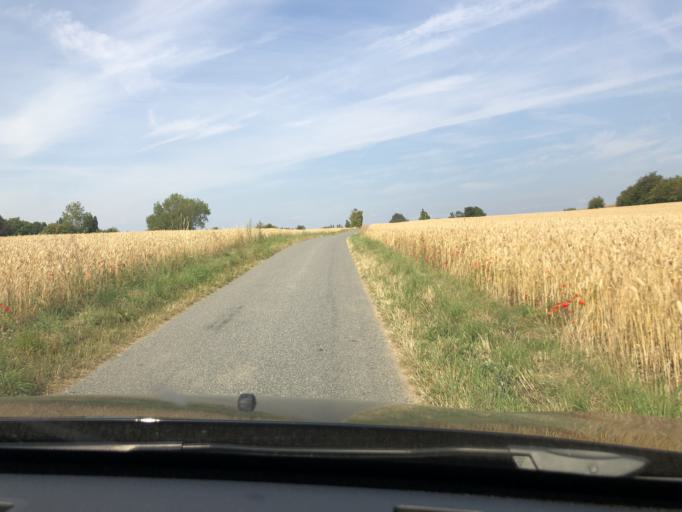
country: DK
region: South Denmark
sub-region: AEro Kommune
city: AEroskobing
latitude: 54.9264
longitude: 10.2790
